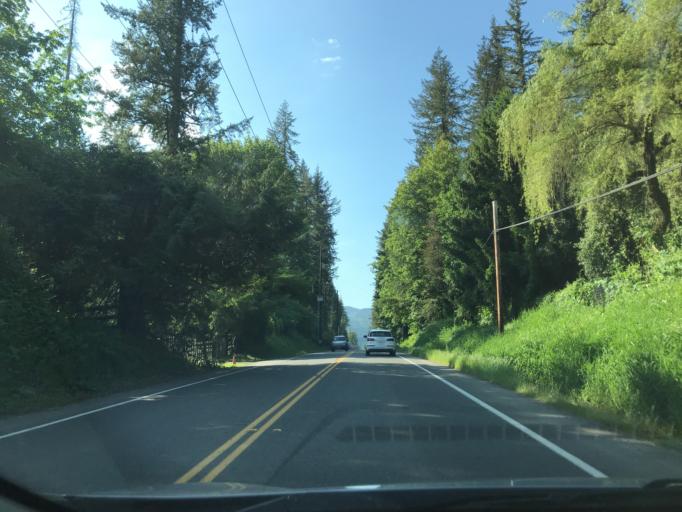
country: US
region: Washington
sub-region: King County
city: Mirrormont
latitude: 47.4642
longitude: -122.0146
